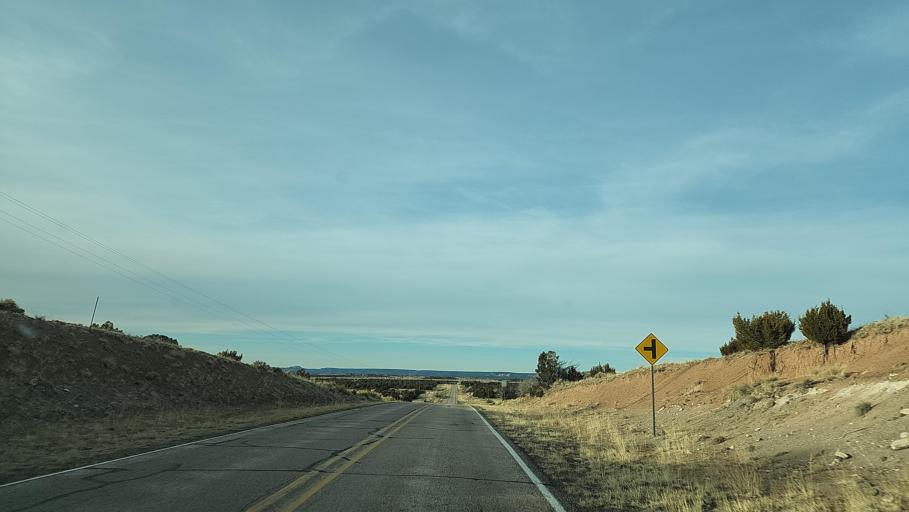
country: US
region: New Mexico
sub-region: McKinley County
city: Black Rock
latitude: 34.4280
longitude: -108.4275
